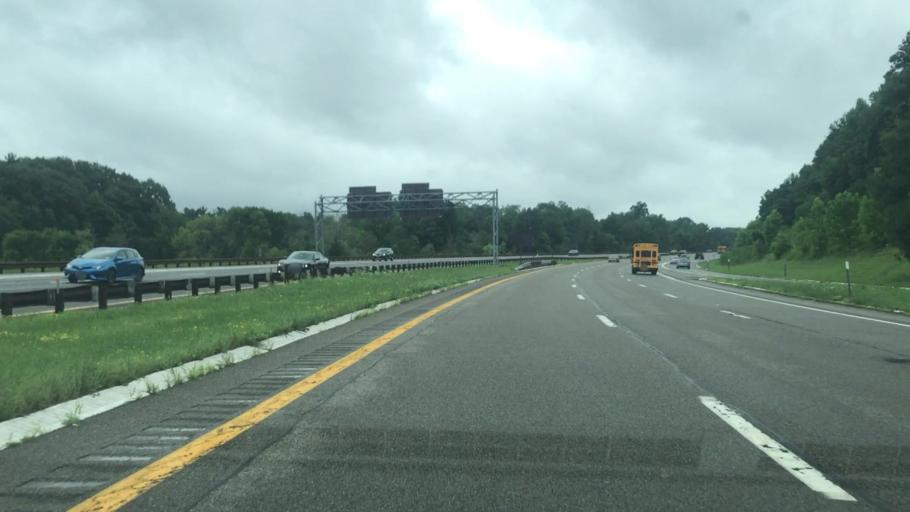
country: US
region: New York
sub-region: Westchester County
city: Jefferson Valley-Yorktown
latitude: 41.2895
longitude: -73.8199
